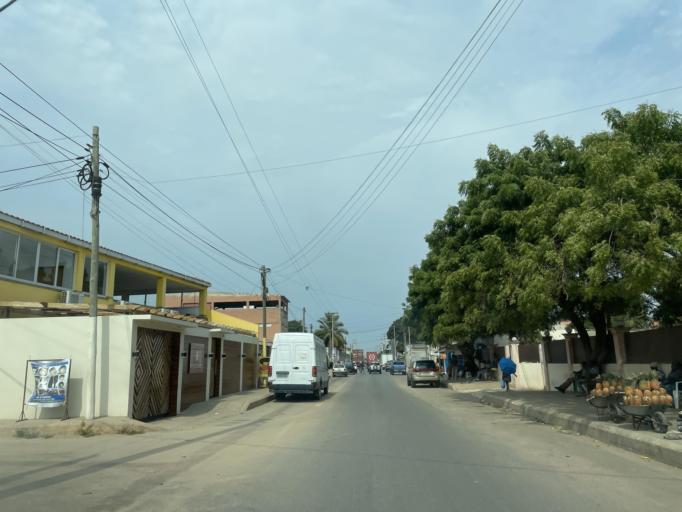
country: AO
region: Luanda
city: Luanda
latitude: -8.8977
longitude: 13.1882
